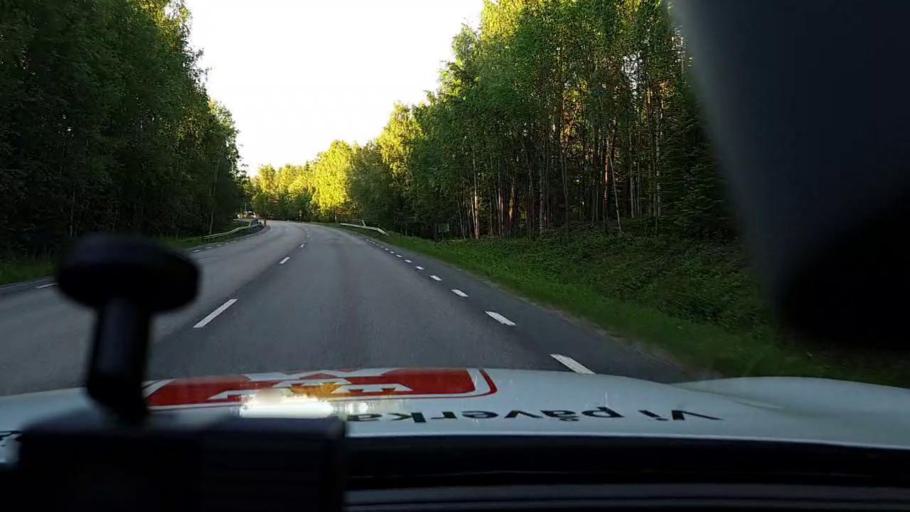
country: SE
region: Norrbotten
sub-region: Lulea Kommun
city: Lulea
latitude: 65.6161
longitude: 22.1992
